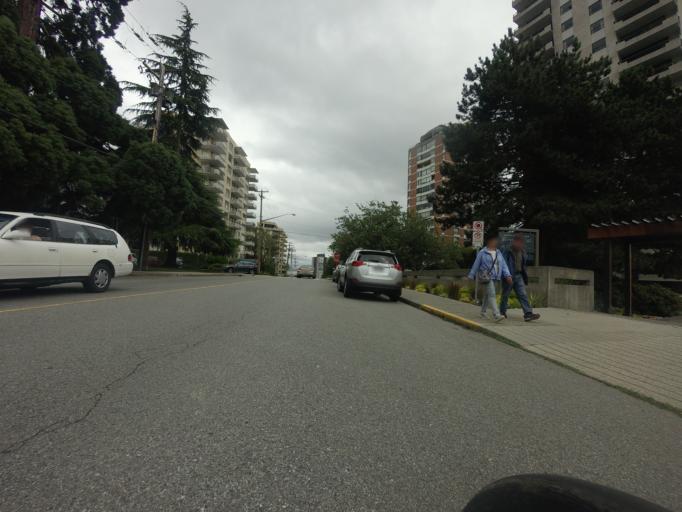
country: CA
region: British Columbia
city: West Vancouver
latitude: 49.3285
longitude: -123.1669
